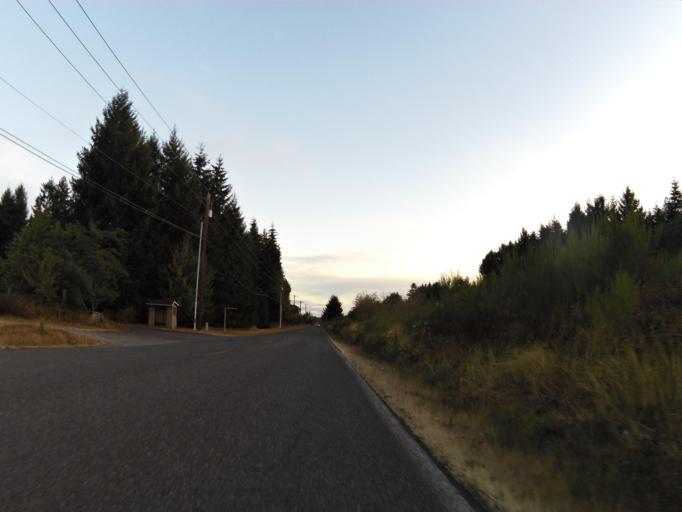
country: US
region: Washington
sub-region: Thurston County
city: Tenino
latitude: 46.8341
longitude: -122.8613
